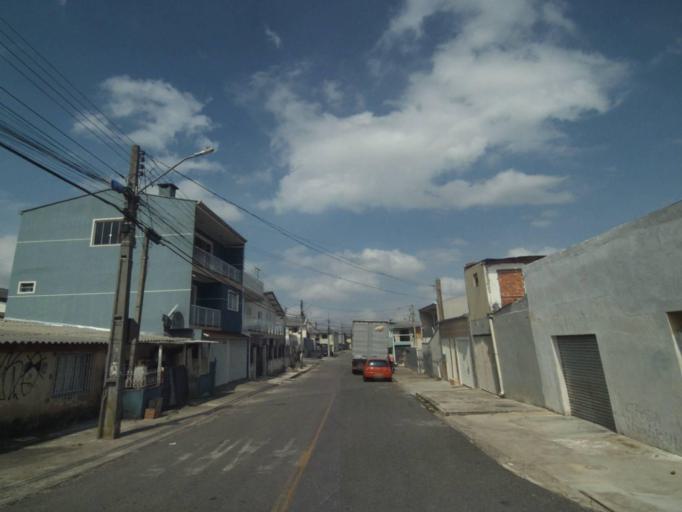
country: BR
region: Parana
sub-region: Curitiba
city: Curitiba
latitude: -25.5008
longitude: -49.3456
